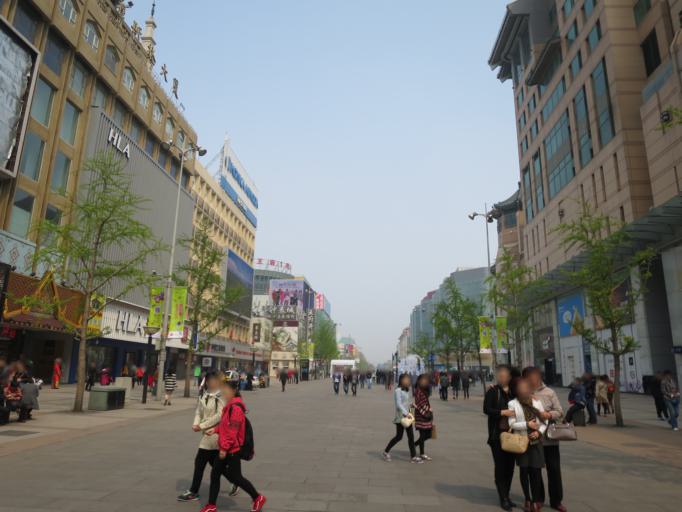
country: CN
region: Beijing
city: Beijing
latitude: 39.9127
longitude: 116.4051
